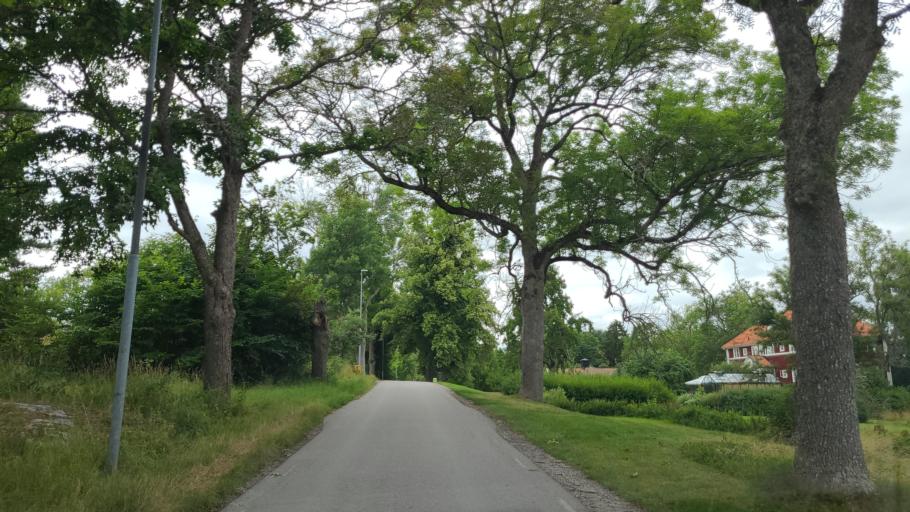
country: SE
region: Stockholm
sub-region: Upplands-Bro Kommun
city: Bro
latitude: 59.5084
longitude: 17.5683
